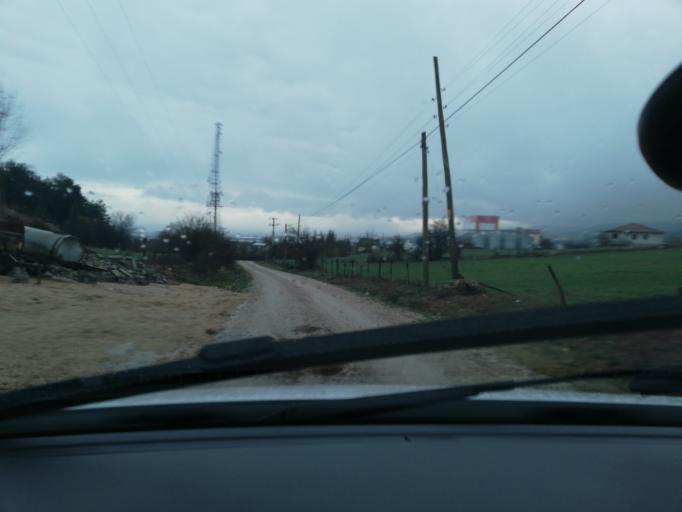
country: TR
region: Bolu
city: Bolu
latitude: 40.7670
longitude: 31.6543
